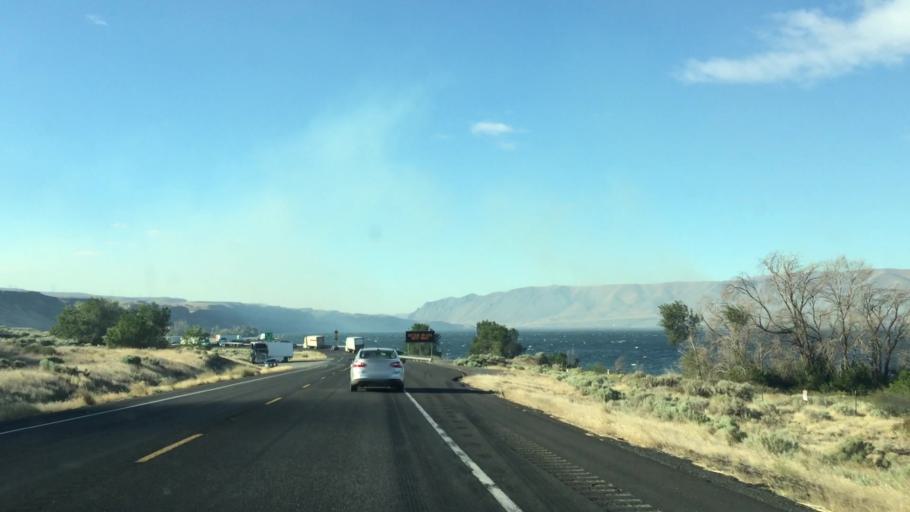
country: US
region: Washington
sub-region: Grant County
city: Mattawa
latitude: 46.9350
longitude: -119.9592
